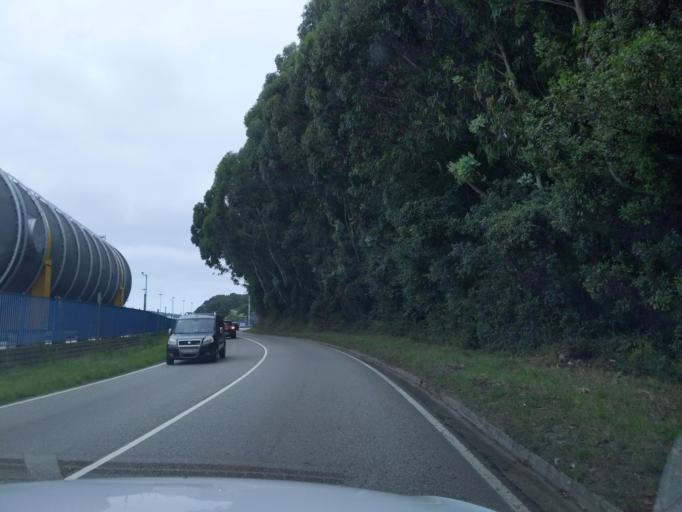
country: ES
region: Asturias
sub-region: Province of Asturias
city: Aviles
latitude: 43.5718
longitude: -5.9173
